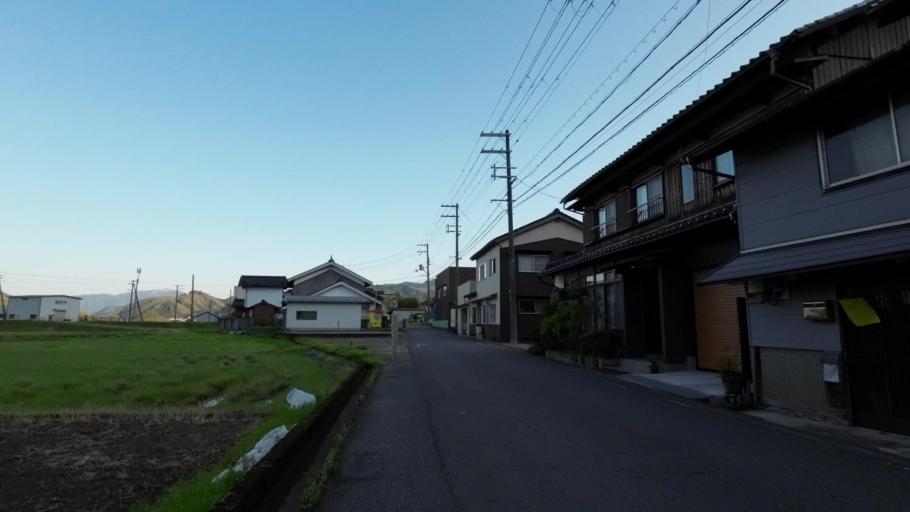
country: JP
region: Hyogo
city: Toyooka
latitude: 35.3731
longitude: 134.8108
